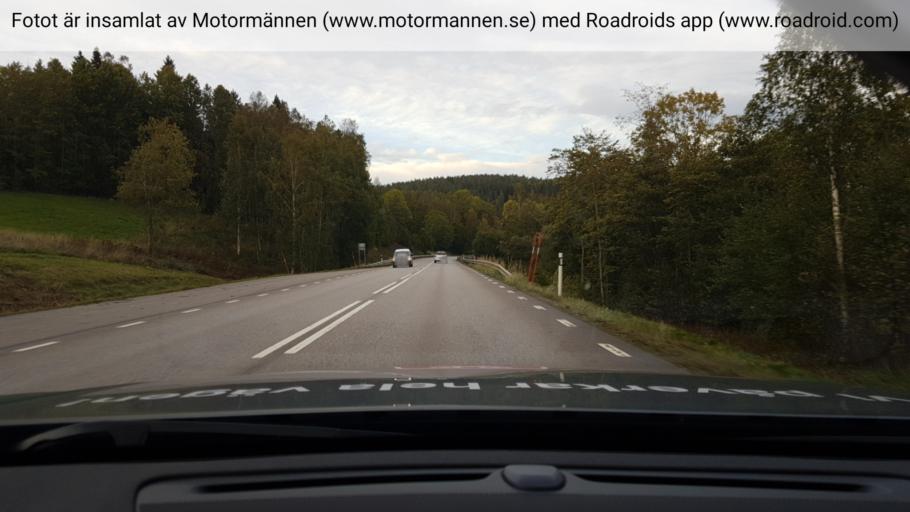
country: SE
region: Vaestra Goetaland
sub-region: Bengtsfors Kommun
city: Billingsfors
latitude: 59.0340
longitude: 12.3130
